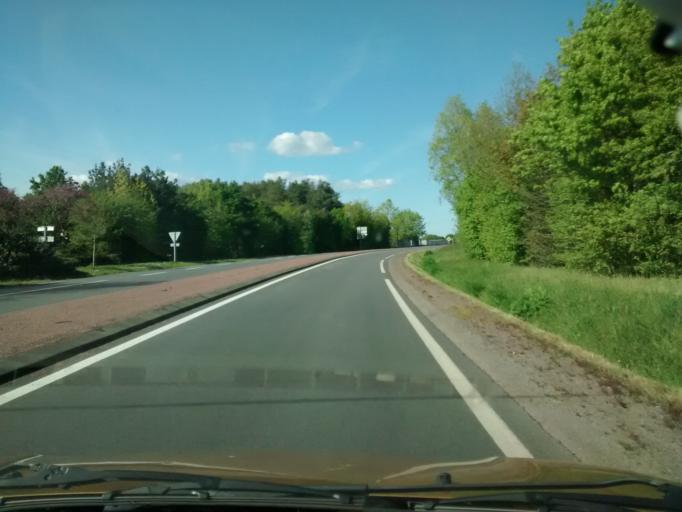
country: FR
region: Pays de la Loire
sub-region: Departement de la Vendee
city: Saint-Philbert-de-Bouaine
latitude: 46.9925
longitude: -1.5161
